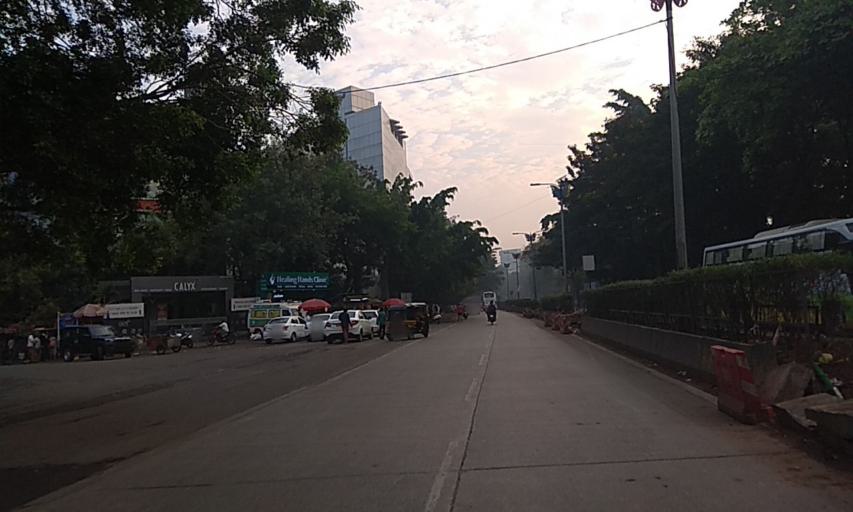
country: IN
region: Maharashtra
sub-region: Pune Division
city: Shivaji Nagar
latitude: 18.5318
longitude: 73.8767
